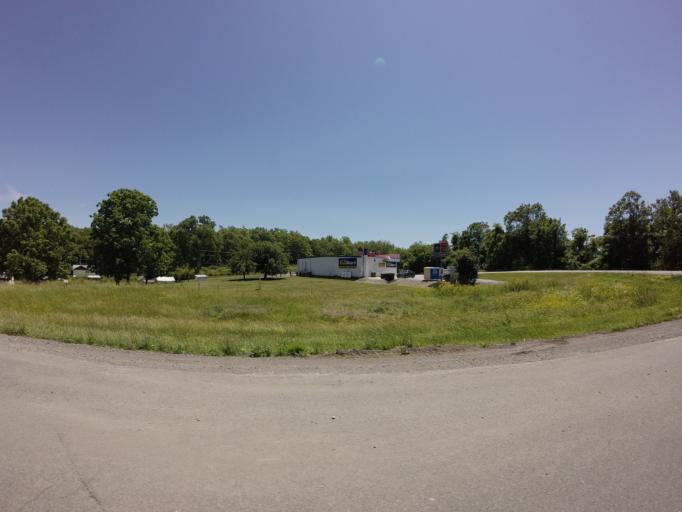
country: US
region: West Virginia
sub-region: Jefferson County
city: Bolivar
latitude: 39.3081
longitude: -77.7995
